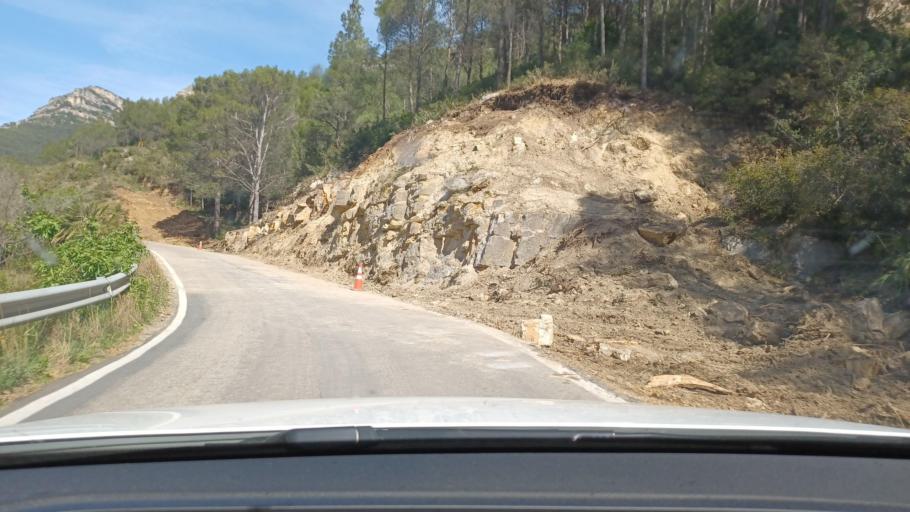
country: ES
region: Valencia
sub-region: Provincia de Castello
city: Rosell
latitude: 40.6702
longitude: 0.2461
